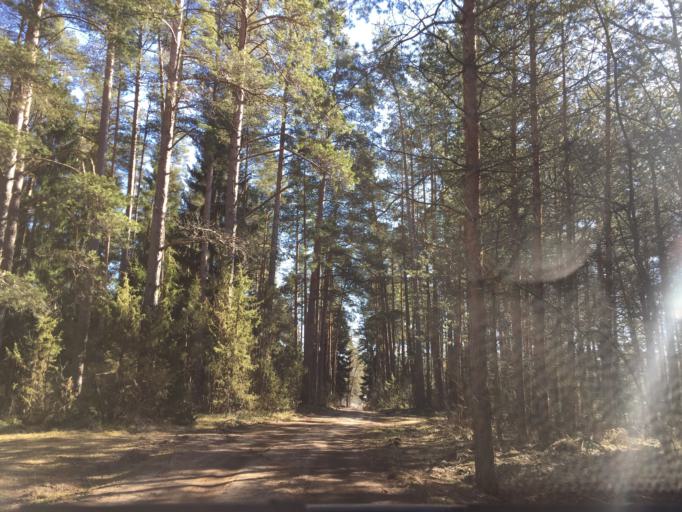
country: LV
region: Incukalns
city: Vangazi
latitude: 57.0919
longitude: 24.5329
